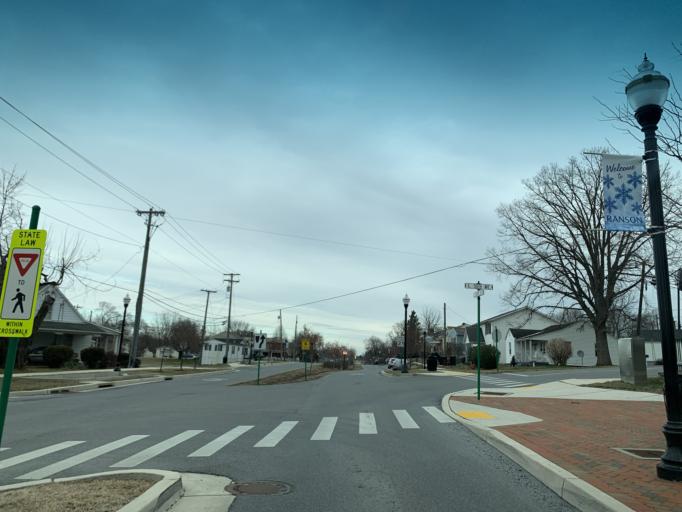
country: US
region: West Virginia
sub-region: Jefferson County
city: Ranson
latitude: 39.2974
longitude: -77.8595
